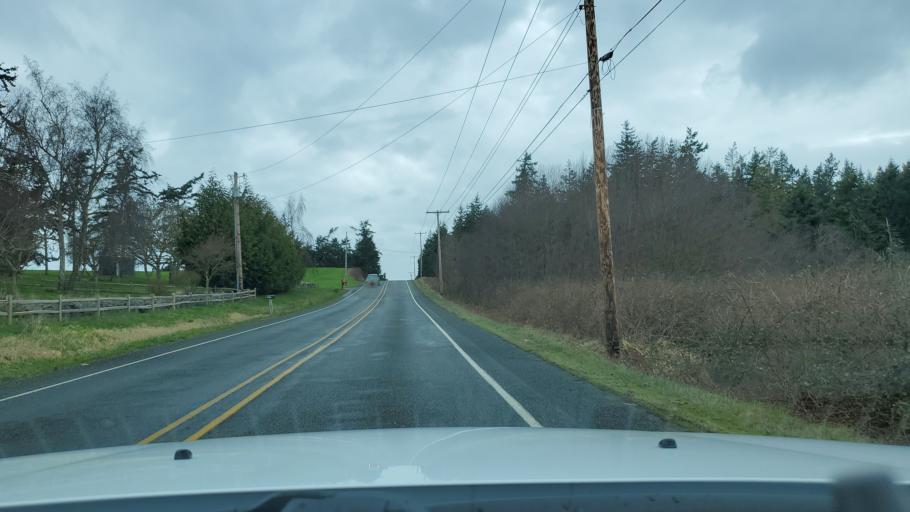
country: US
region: Washington
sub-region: Island County
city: Ault Field
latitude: 48.3079
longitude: -122.7043
